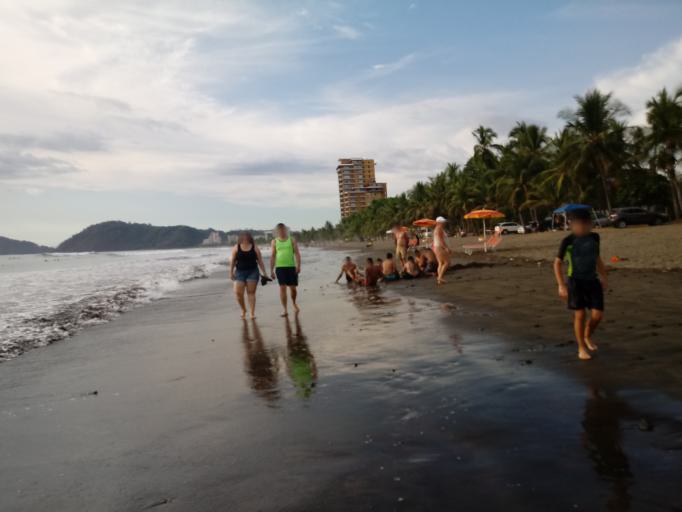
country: CR
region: Puntarenas
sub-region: Canton de Garabito
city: Jaco
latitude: 9.6071
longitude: -84.6248
